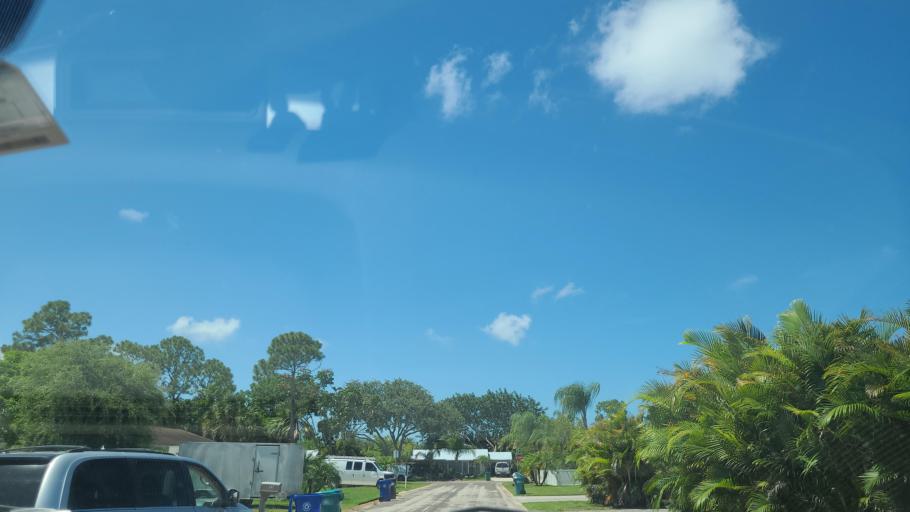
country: US
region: Florida
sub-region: Indian River County
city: Sebastian
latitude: 27.7840
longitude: -80.4694
